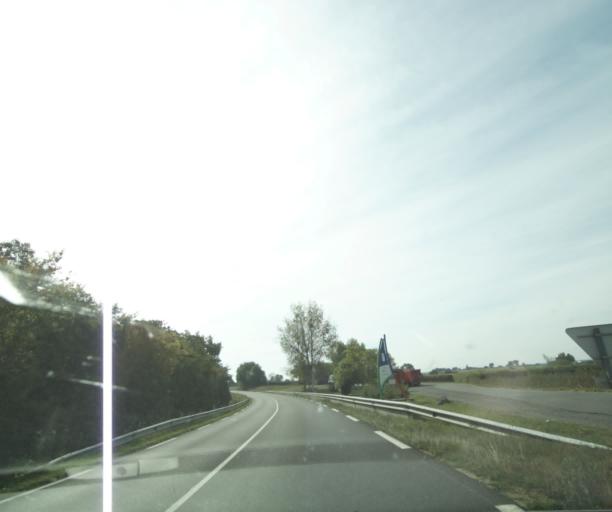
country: FR
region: Auvergne
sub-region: Departement de l'Allier
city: Saint-Francois
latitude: 46.4348
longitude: 3.9072
